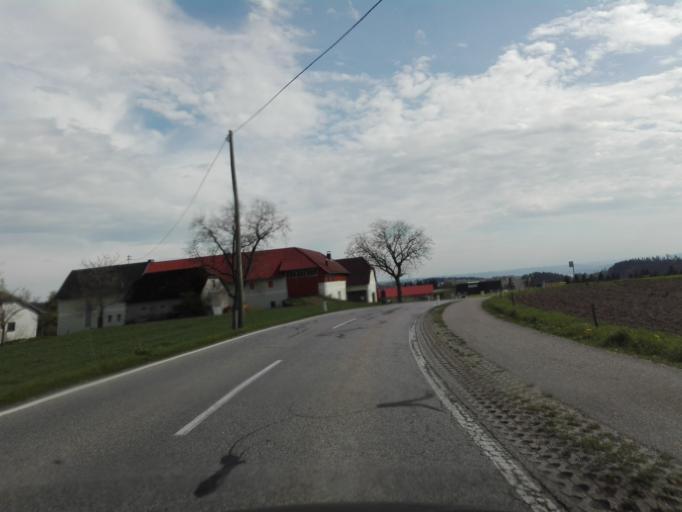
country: AT
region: Upper Austria
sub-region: Politischer Bezirk Rohrbach
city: Kleinzell im Muehlkreis
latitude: 48.4312
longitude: 14.0325
